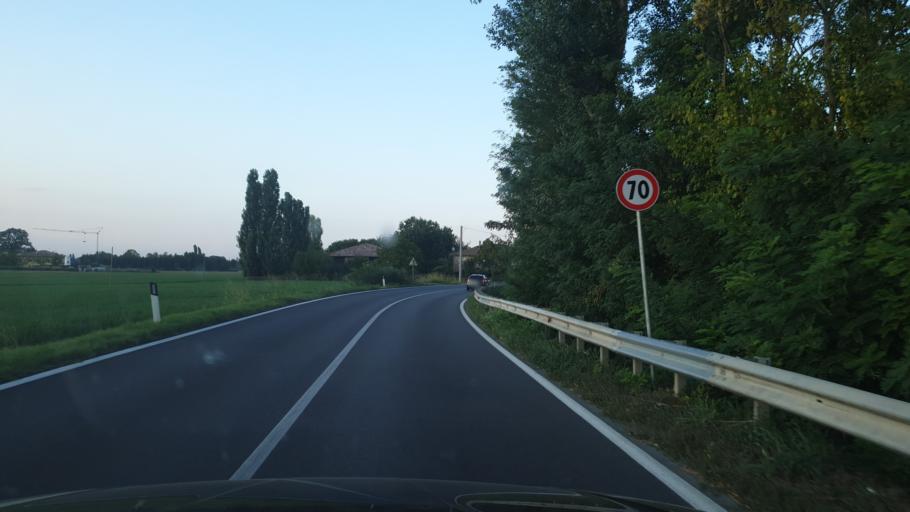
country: IT
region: Emilia-Romagna
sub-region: Provincia di Bologna
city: Progresso
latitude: 44.5522
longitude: 11.3878
